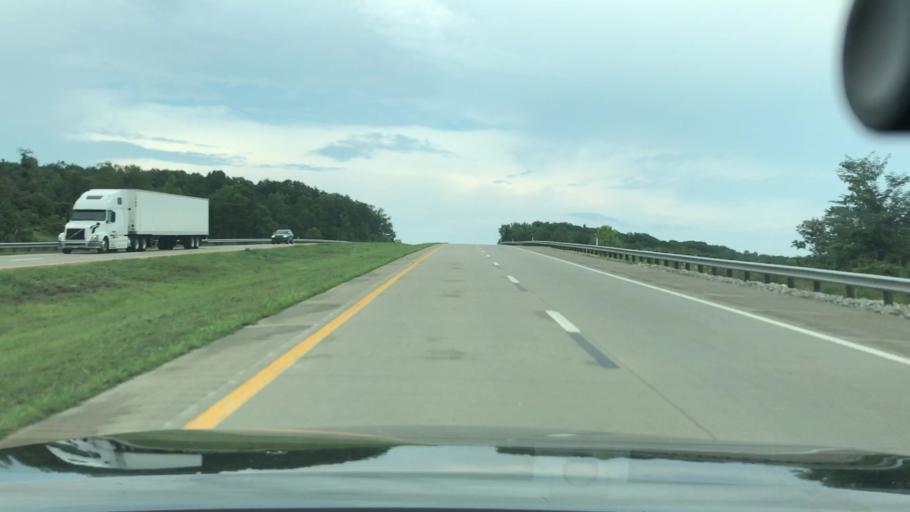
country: US
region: West Virginia
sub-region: Mason County
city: Point Pleasant
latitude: 38.7765
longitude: -82.0600
